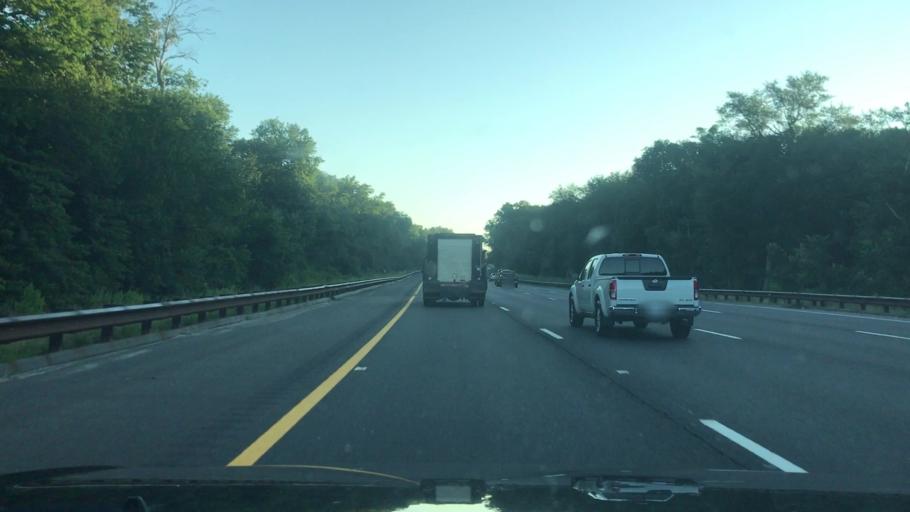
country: US
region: New Jersey
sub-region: Monmouth County
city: Ramtown
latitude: 40.1411
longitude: -74.1111
